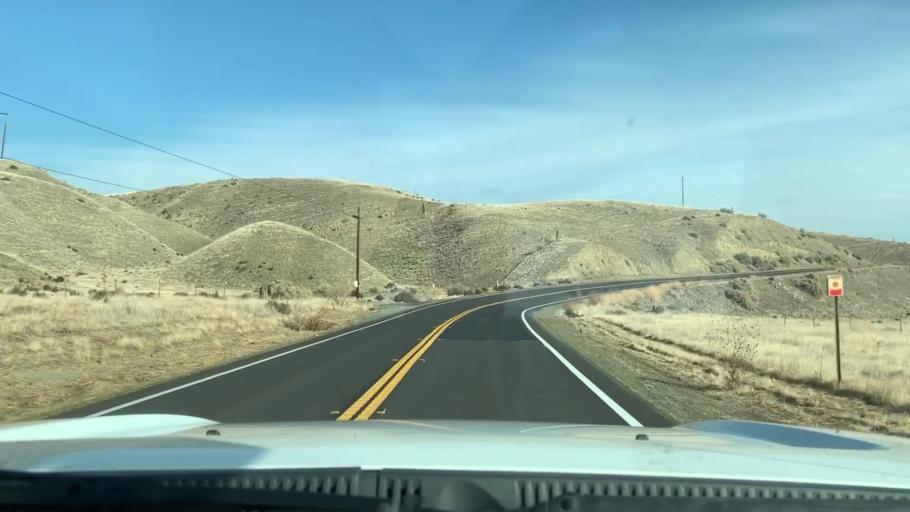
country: US
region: California
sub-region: Fresno County
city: Coalinga
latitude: 36.1129
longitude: -120.3882
